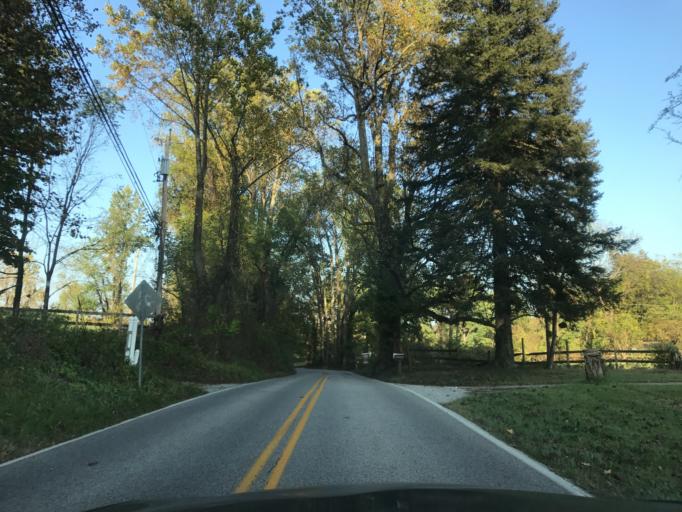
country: US
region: Maryland
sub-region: Anne Arundel County
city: Crownsville
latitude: 39.0448
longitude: -76.6348
